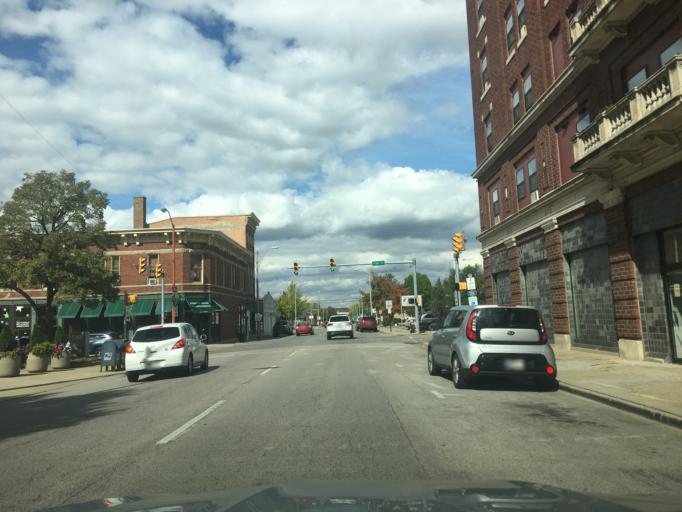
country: US
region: Indiana
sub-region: Tippecanoe County
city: West Lafayette
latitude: 40.4197
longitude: -86.8931
